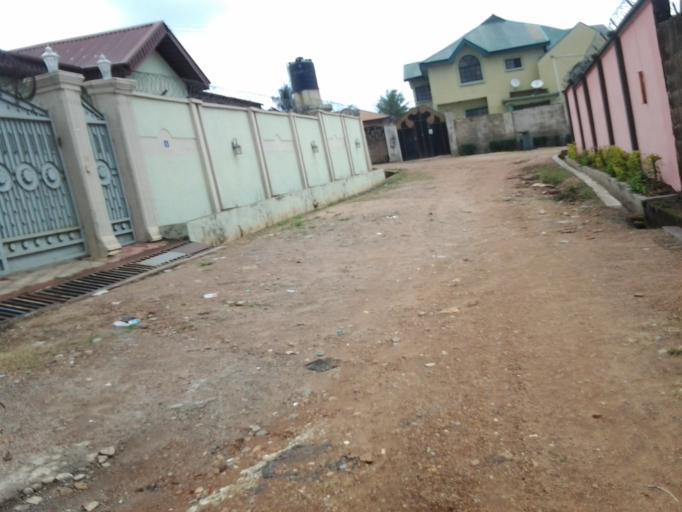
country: NG
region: Oyo
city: Ibadan
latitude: 7.4392
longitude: 3.9572
